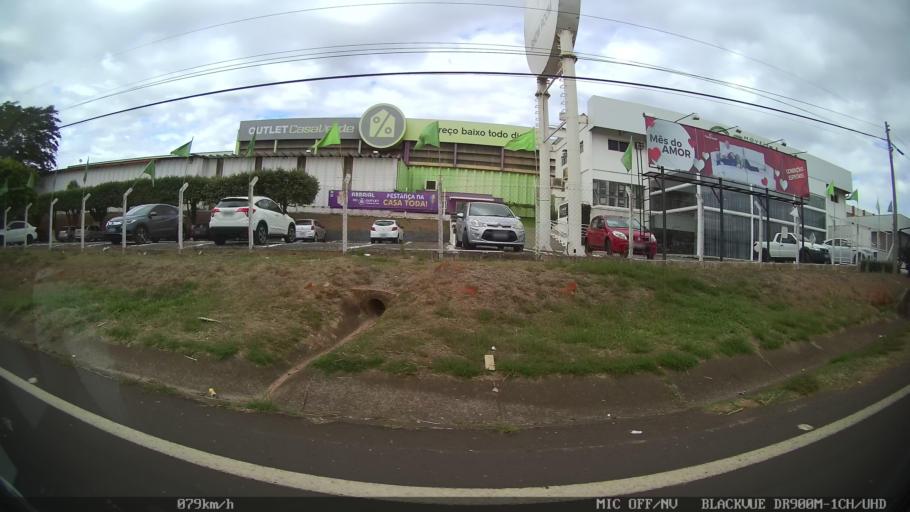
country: BR
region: Sao Paulo
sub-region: Sao Jose Do Rio Preto
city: Sao Jose do Rio Preto
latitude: -20.8122
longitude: -49.4857
